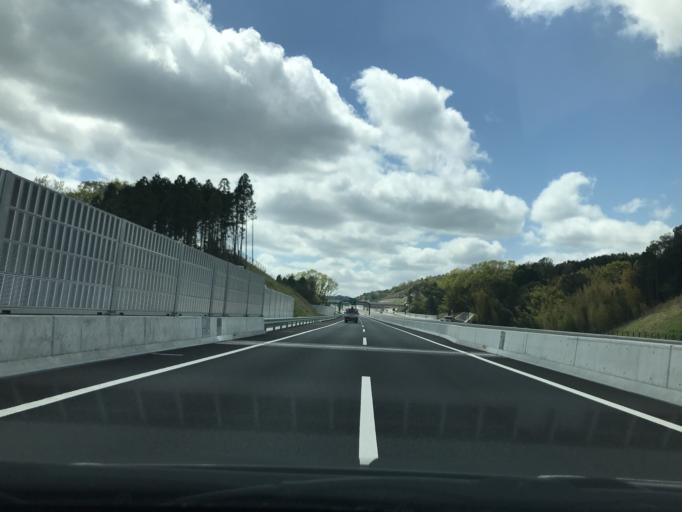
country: JP
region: Osaka
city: Ibaraki
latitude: 34.8888
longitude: 135.5403
